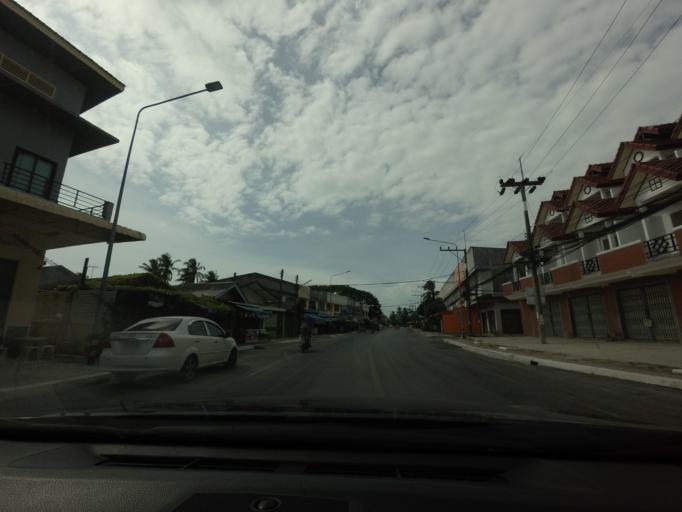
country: TH
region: Pattani
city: Pattani
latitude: 6.8770
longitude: 101.2479
